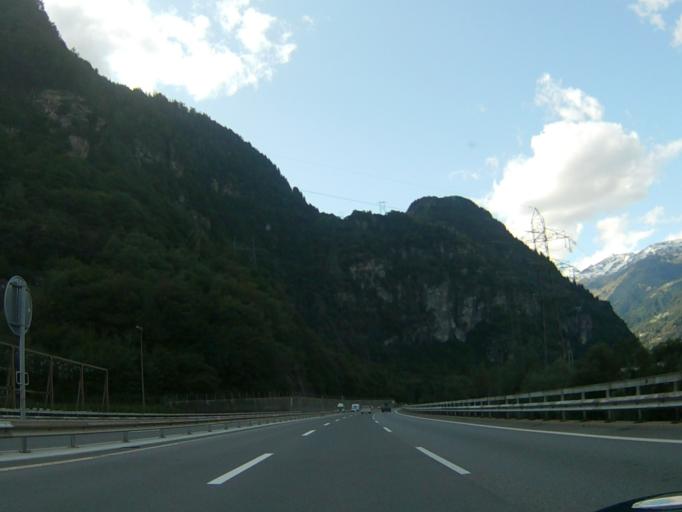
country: CH
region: Ticino
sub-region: Leventina District
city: Faido
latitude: 46.4380
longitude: 8.8403
